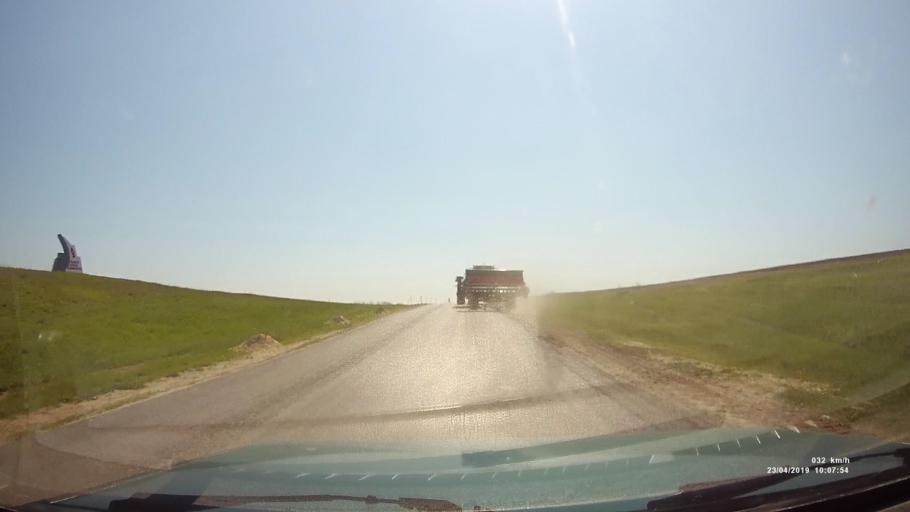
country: RU
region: Rostov
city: Sovetskoye
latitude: 46.7222
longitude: 42.2597
